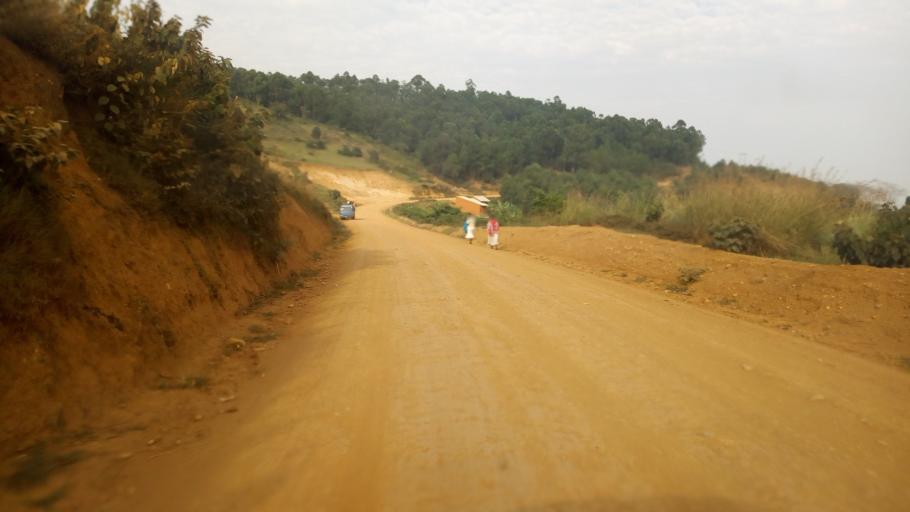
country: UG
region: Western Region
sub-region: Kanungu District
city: Ntungamo
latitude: -0.8306
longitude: 29.6974
